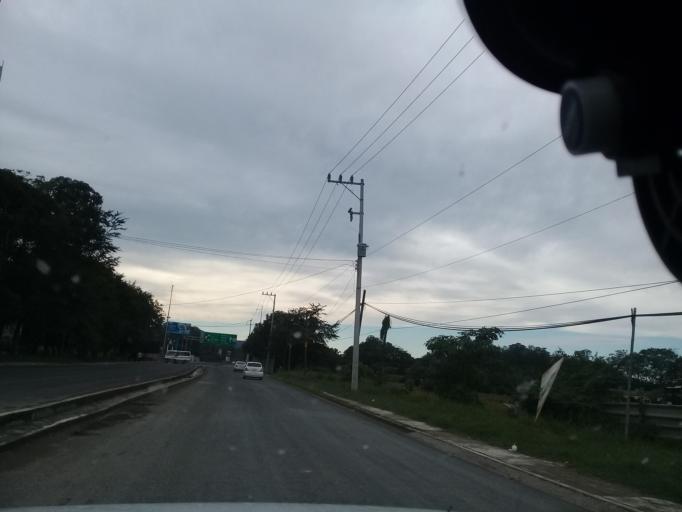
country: MX
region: Hidalgo
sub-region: Huejutla de Reyes
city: Parque de Poblamiento Solidaridad
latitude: 21.1539
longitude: -98.3861
